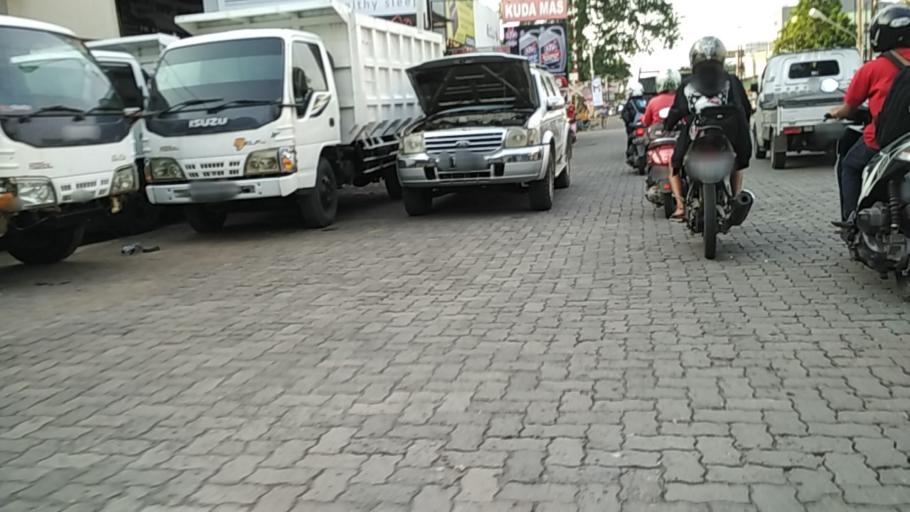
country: ID
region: Central Java
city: Semarang
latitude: -6.9793
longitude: 110.3910
